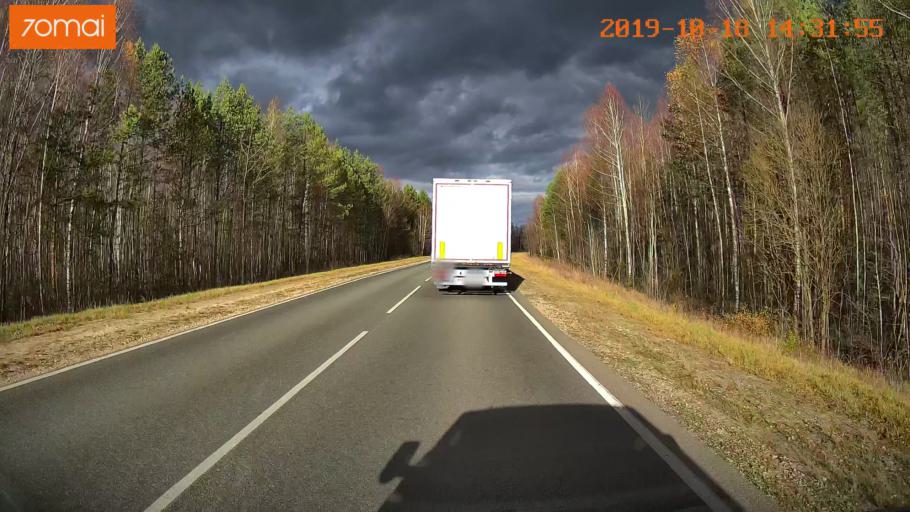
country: RU
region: Rjazan
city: Tuma
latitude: 55.1871
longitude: 40.5734
